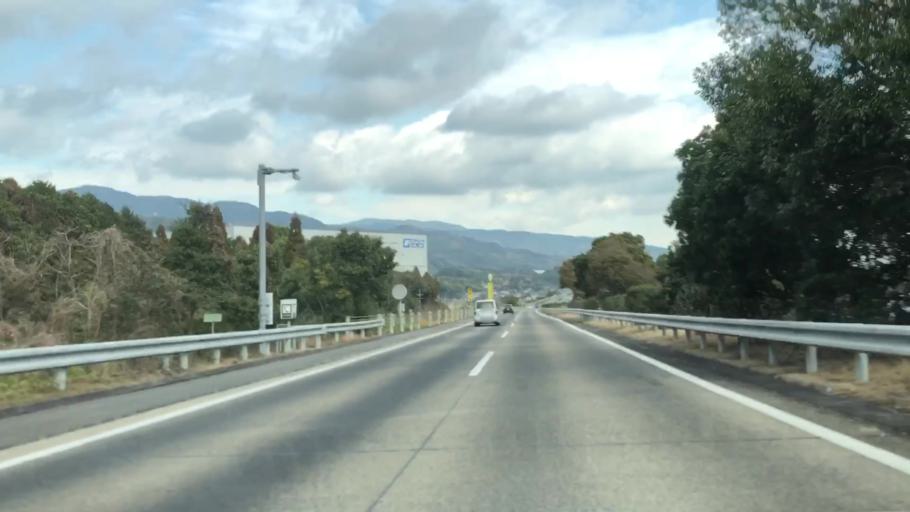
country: JP
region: Saga Prefecture
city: Kanzakimachi-kanzaki
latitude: 33.3426
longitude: 130.3588
